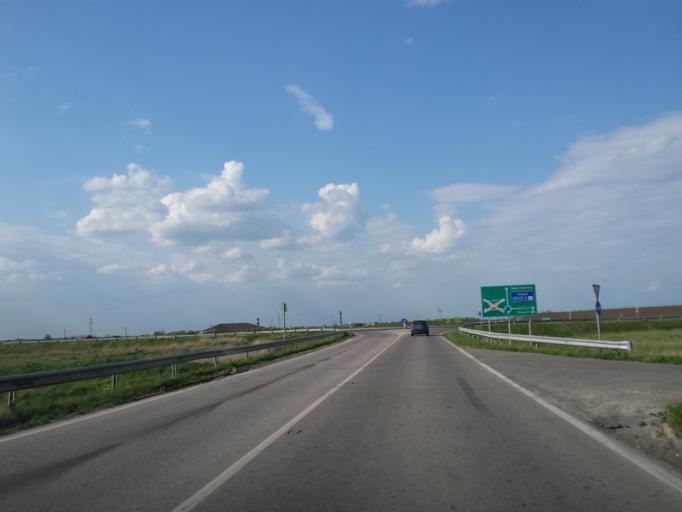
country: HU
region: Csongrad
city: Mako
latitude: 46.2421
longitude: 20.4813
